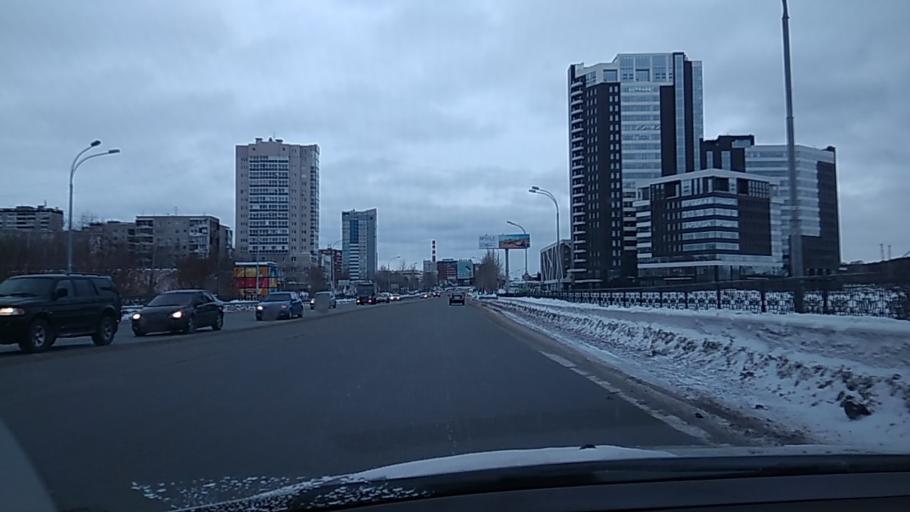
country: RU
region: Sverdlovsk
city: Yekaterinburg
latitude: 56.8173
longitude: 60.6272
